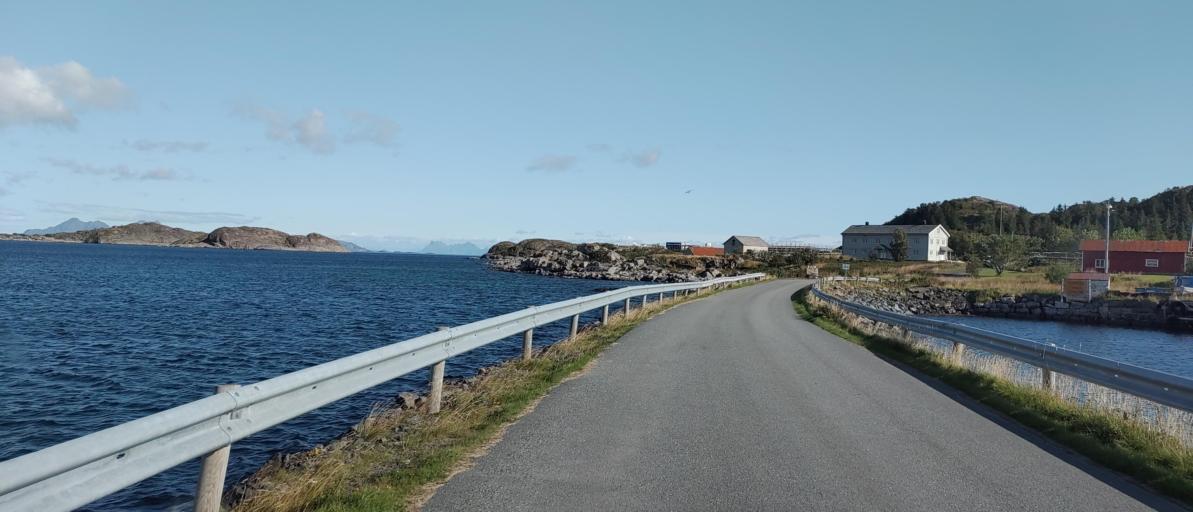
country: NO
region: Nordland
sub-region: Vagan
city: Kabelvag
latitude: 68.1609
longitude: 14.2202
